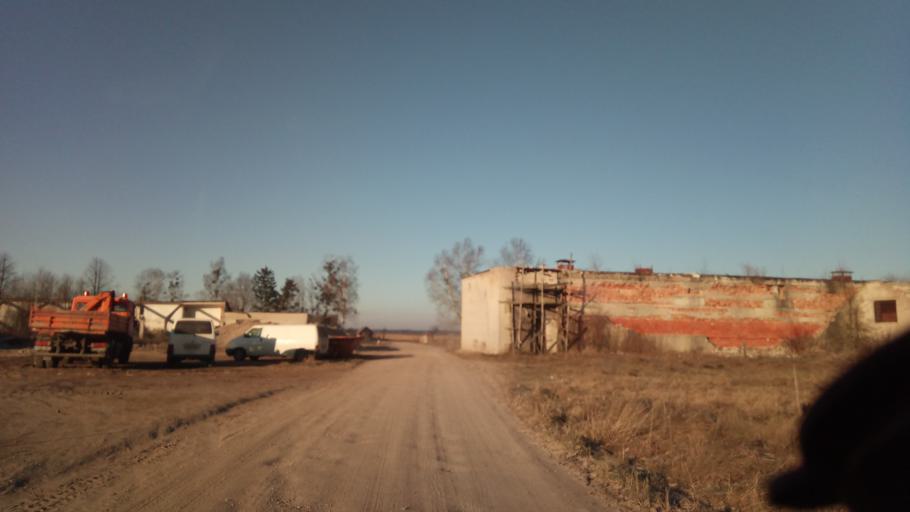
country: LT
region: Alytaus apskritis
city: Druskininkai
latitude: 54.0876
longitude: 23.9814
